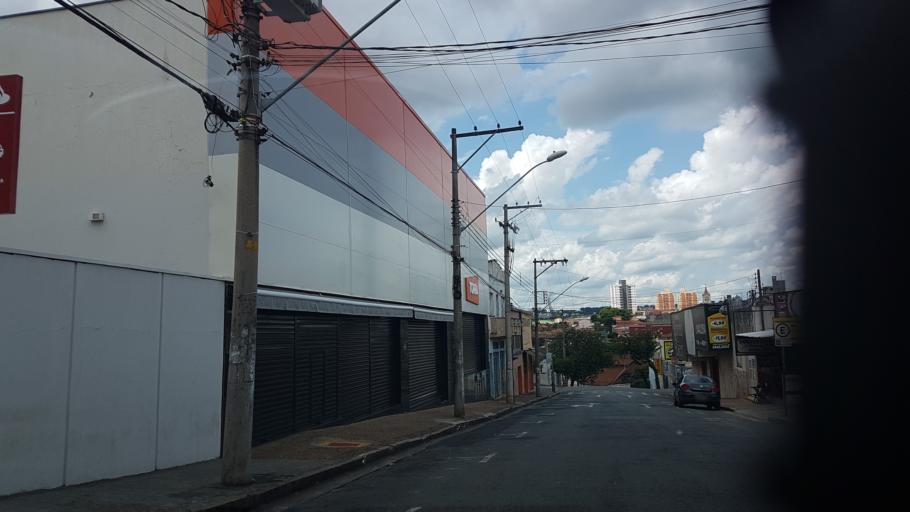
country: BR
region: Sao Paulo
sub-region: Limeira
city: Limeira
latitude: -22.5633
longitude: -47.4001
